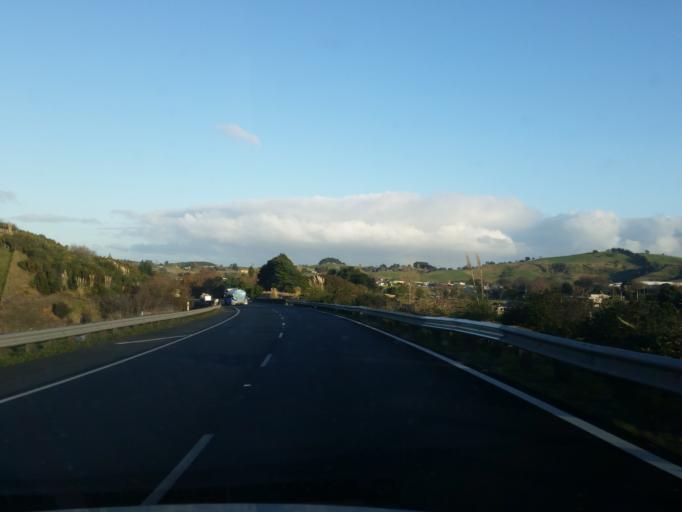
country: NZ
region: Auckland
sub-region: Auckland
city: Pukekohe East
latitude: -37.2387
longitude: 175.0208
